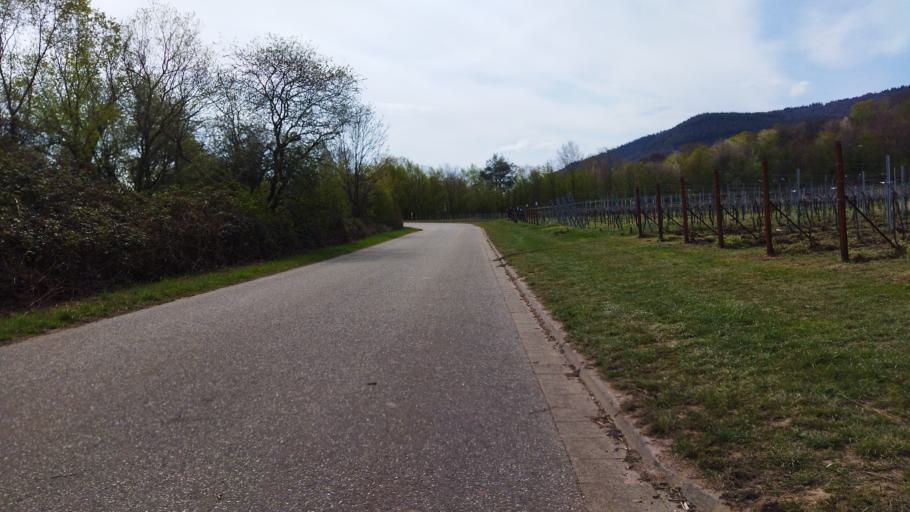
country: DE
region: Rheinland-Pfalz
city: Rhodt unter Rietburg
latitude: 49.2777
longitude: 8.0945
